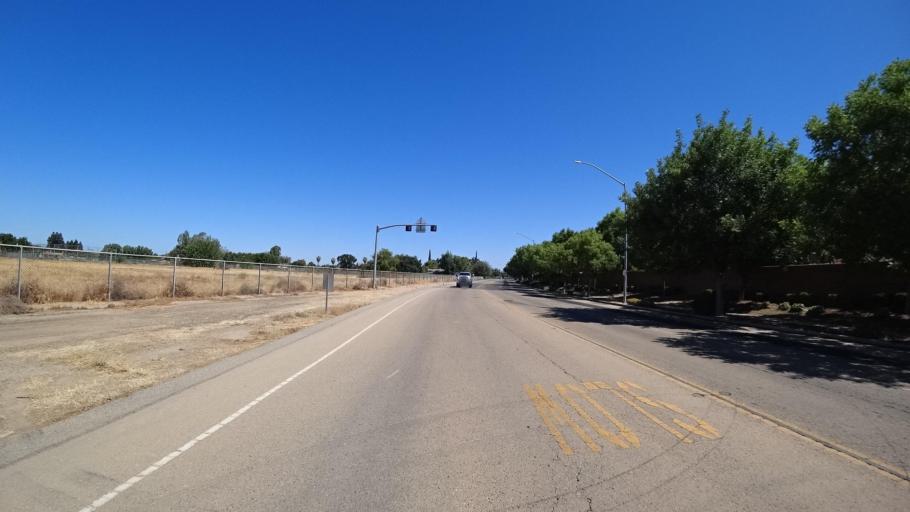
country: US
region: California
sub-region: Fresno County
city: Sunnyside
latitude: 36.7339
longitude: -119.6731
